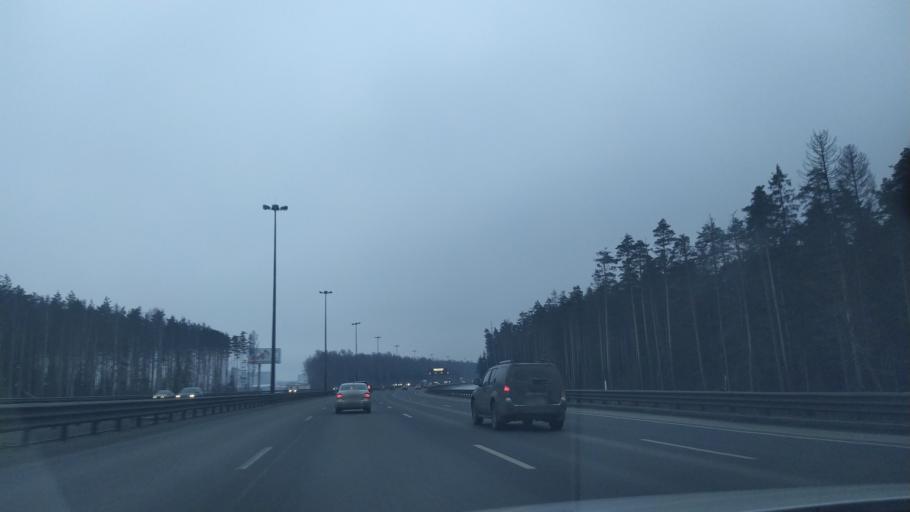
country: RU
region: Leningrad
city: Yanino Vtoroye
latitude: 59.9619
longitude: 30.5538
